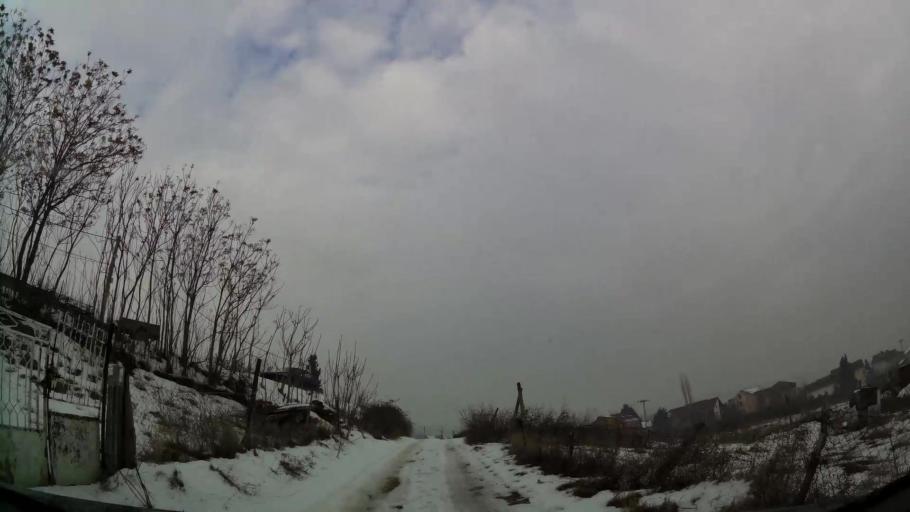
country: MK
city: Kondovo
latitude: 42.0420
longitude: 21.3439
